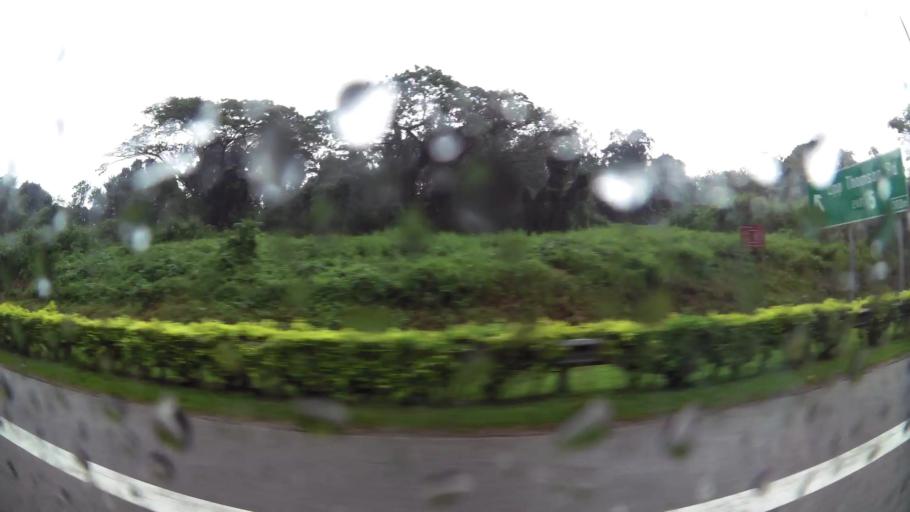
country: MY
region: Johor
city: Kampung Pasir Gudang Baru
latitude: 1.3928
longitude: 103.8249
